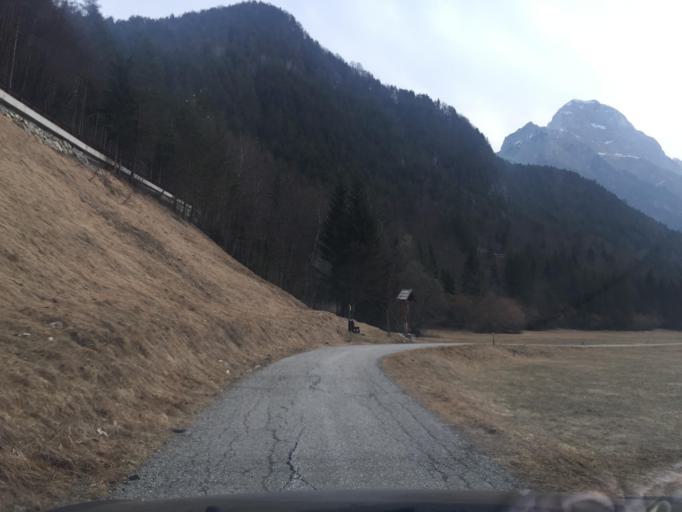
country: SI
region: Bovec
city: Bovec
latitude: 46.4085
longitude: 13.6058
